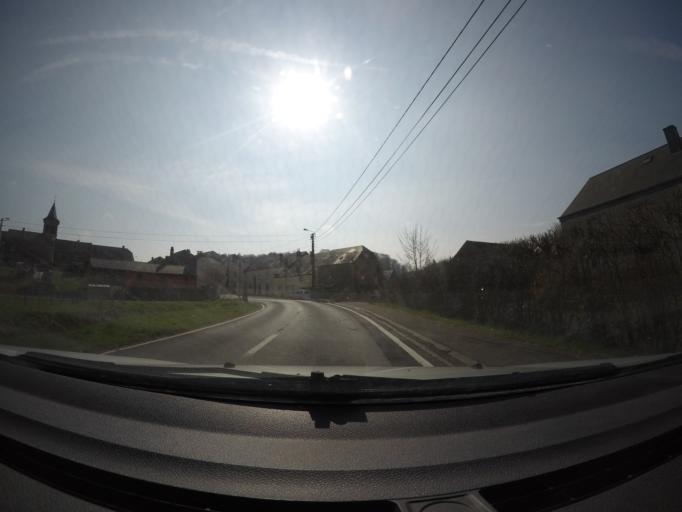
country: BE
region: Wallonia
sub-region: Province du Luxembourg
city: Tintigny
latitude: 49.7174
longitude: 5.4833
